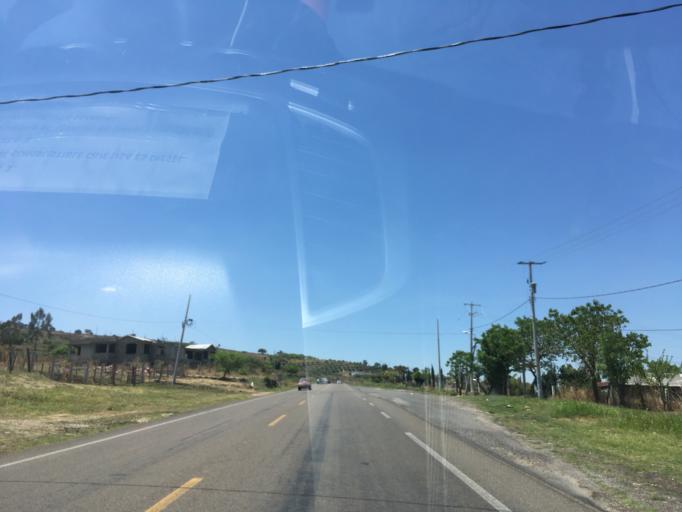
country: MX
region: Michoacan
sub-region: Tuxpan
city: La Soledad
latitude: 19.5289
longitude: -100.4741
